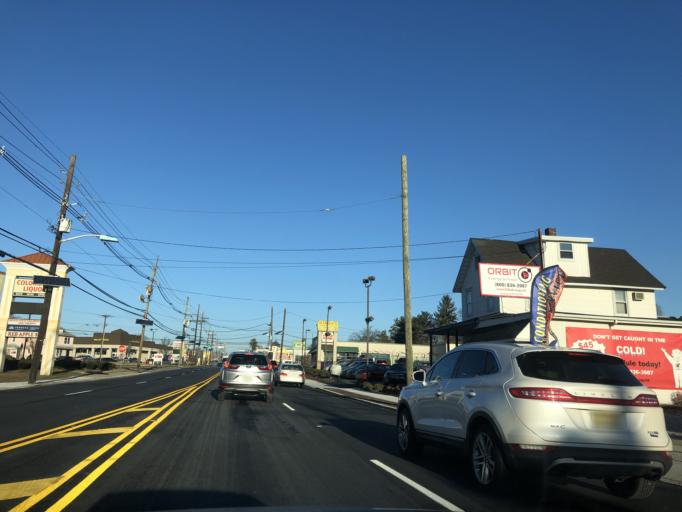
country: US
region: New Jersey
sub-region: Camden County
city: Lawnside
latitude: 39.8603
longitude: -75.0322
